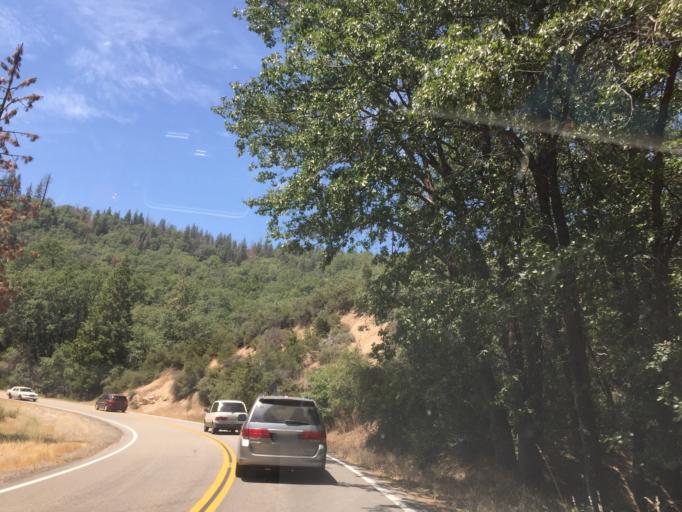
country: US
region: California
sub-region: Fresno County
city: Squaw Valley
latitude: 36.8171
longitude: -118.9137
